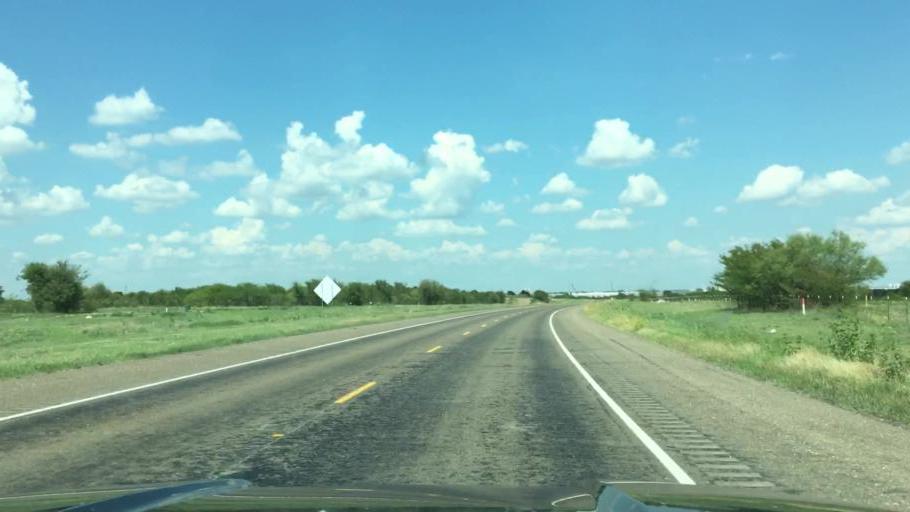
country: US
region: Texas
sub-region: Tarrant County
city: Haslet
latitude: 33.0103
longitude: -97.3395
